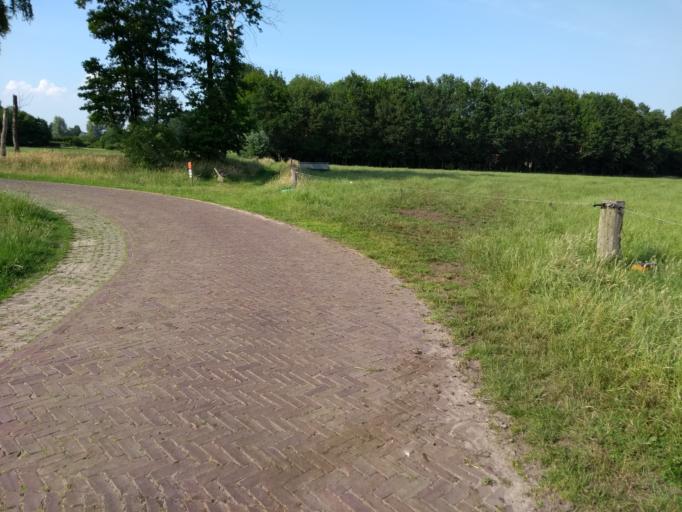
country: NL
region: Overijssel
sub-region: Gemeente Tubbergen
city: Tubbergen
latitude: 52.3670
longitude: 6.7507
